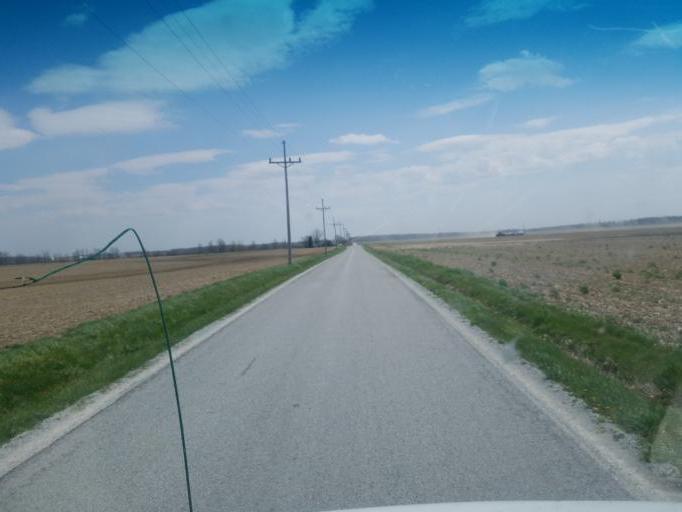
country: US
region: Ohio
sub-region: Hardin County
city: Forest
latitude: 40.7597
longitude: -83.5210
